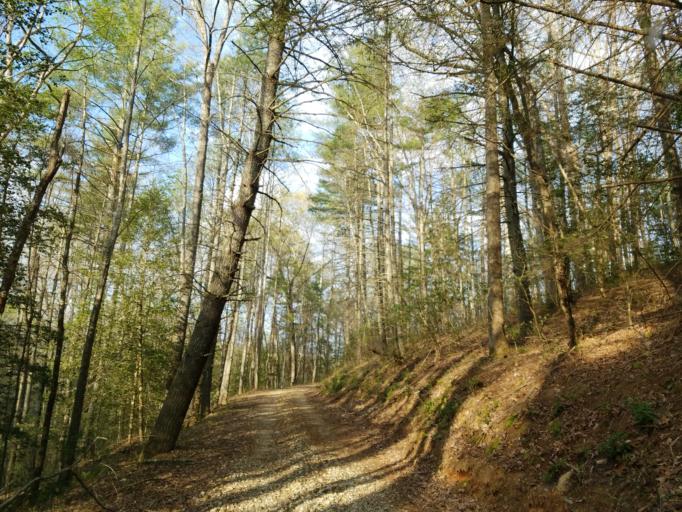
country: US
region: Georgia
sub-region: Fannin County
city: Blue Ridge
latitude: 34.7230
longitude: -84.2034
